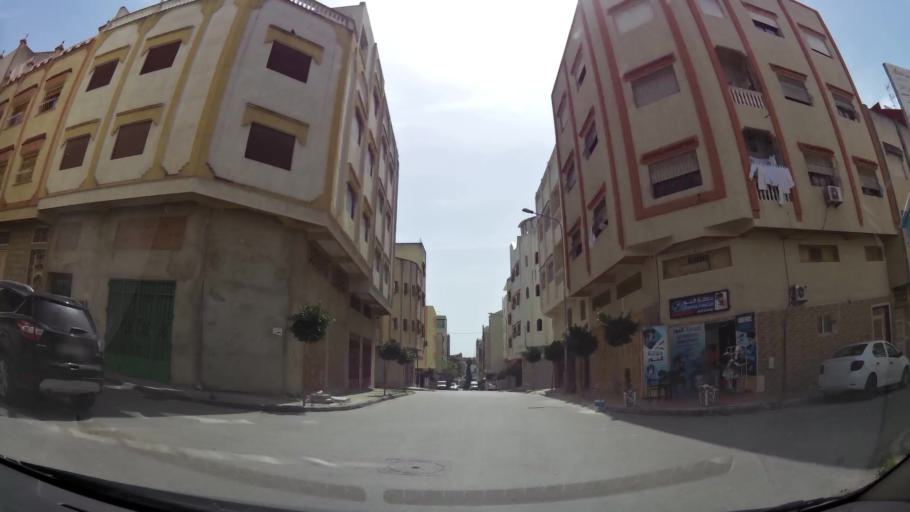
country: MA
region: Tanger-Tetouan
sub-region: Tanger-Assilah
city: Tangier
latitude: 35.7484
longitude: -5.8385
